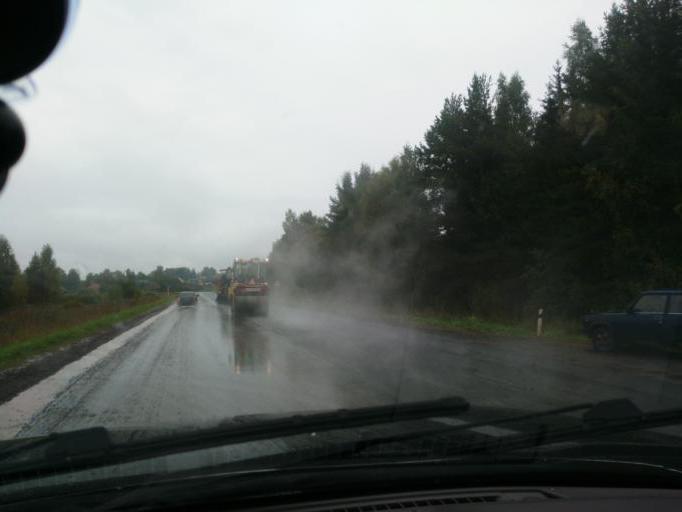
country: RU
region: Perm
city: Osa
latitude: 57.3641
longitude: 55.6036
